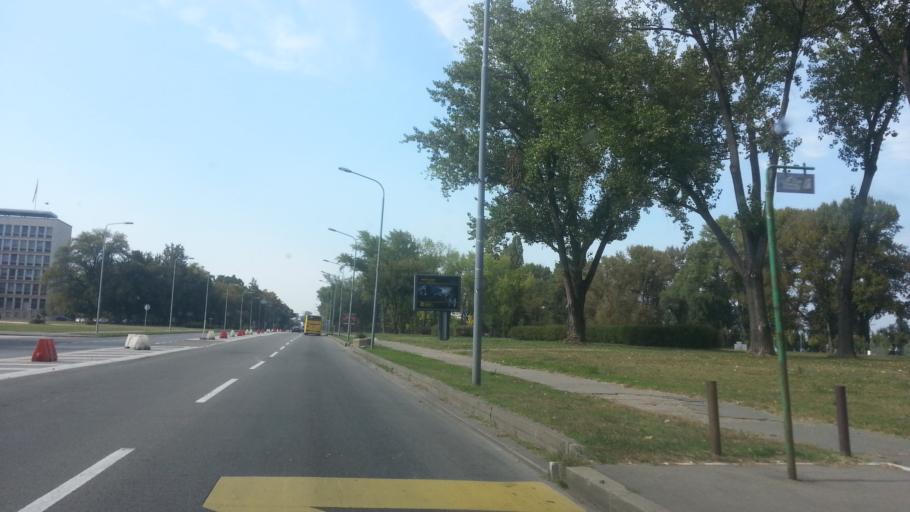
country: RS
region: Central Serbia
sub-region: Belgrade
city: Novi Beograd
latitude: 44.8210
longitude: 20.4303
